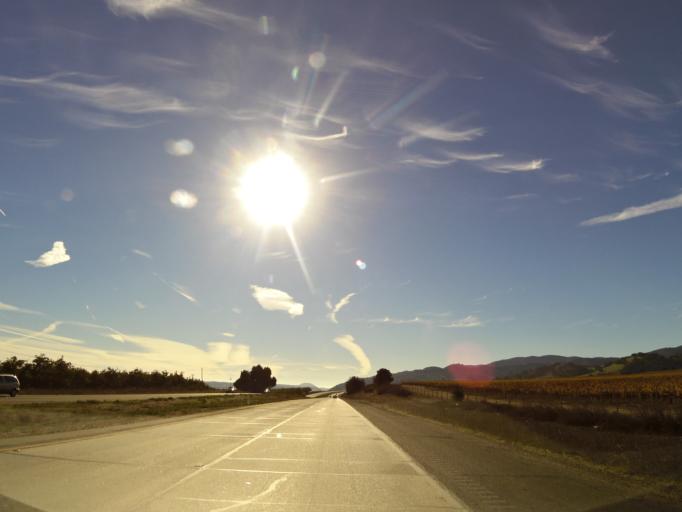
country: US
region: California
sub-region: San Luis Obispo County
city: Lake Nacimiento
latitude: 35.9924
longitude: -120.9077
